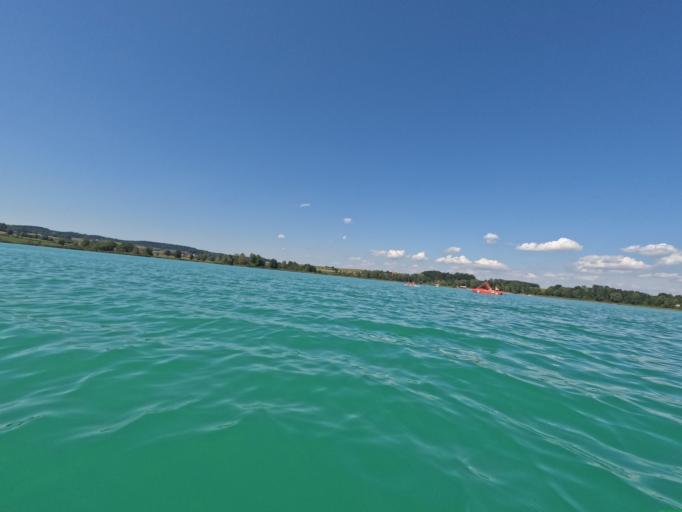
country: DE
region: Bavaria
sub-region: Upper Bavaria
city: Taching am See
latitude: 47.9812
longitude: 12.7448
